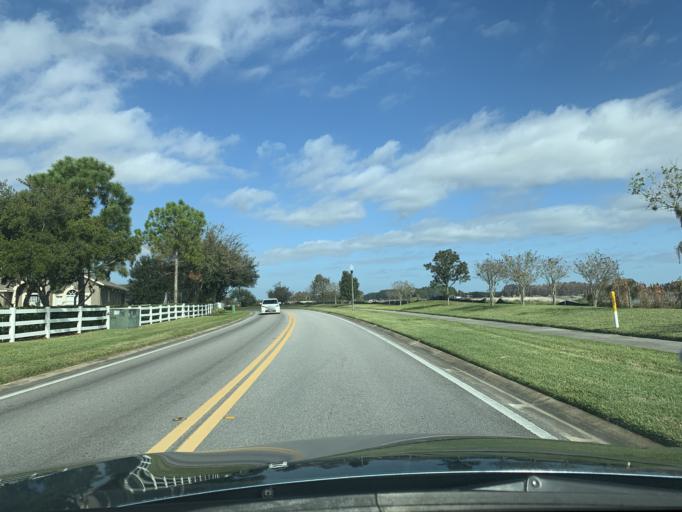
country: US
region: Florida
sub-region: Pasco County
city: Trinity
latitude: 28.1967
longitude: -82.6793
